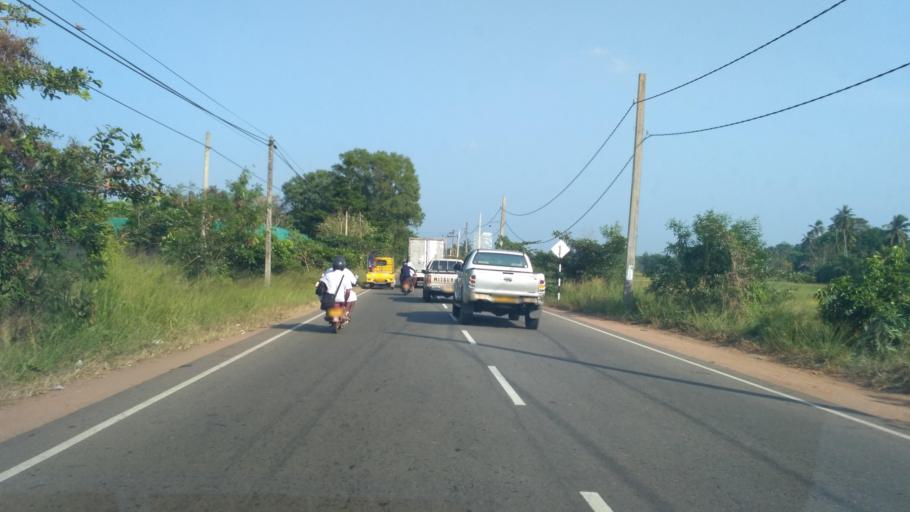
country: LK
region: North Western
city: Kuliyapitiya
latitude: 7.3271
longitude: 80.0279
